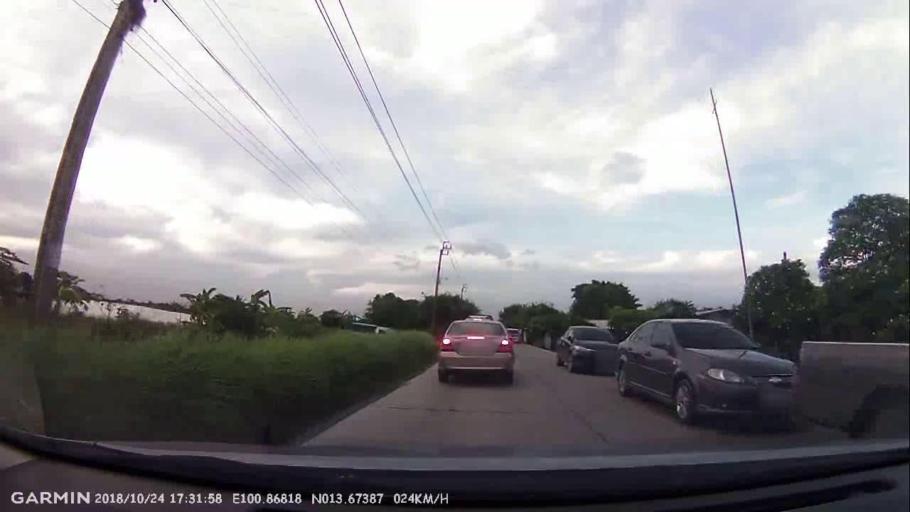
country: TH
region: Samut Prakan
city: Ban Khlong Bang Sao Thong
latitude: 13.6736
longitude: 100.8683
